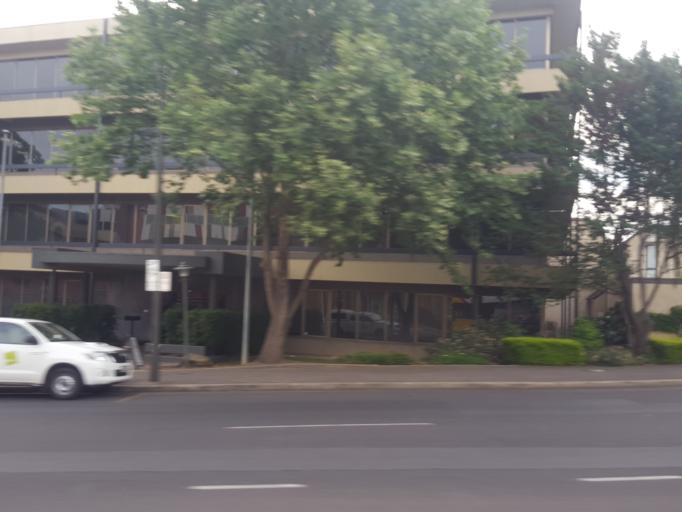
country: AU
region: South Australia
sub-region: Adelaide
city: North Adelaide
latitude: -34.9108
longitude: 138.5992
